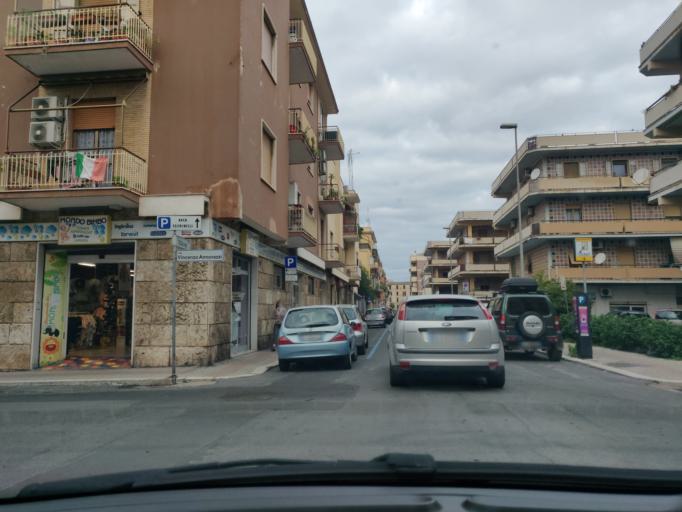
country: IT
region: Latium
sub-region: Citta metropolitana di Roma Capitale
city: Civitavecchia
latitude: 42.0914
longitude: 11.7992
